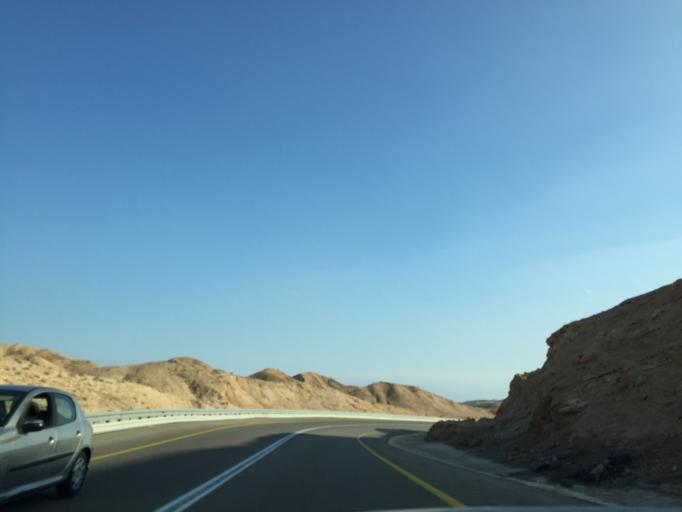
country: IL
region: Southern District
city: `En Boqeq
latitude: 31.1873
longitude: 35.2880
